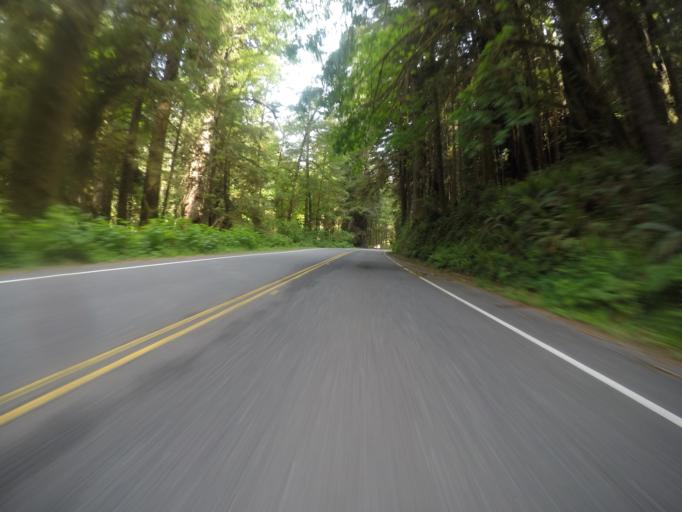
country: US
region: California
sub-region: Del Norte County
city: Bertsch-Oceanview
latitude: 41.4183
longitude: -124.0336
